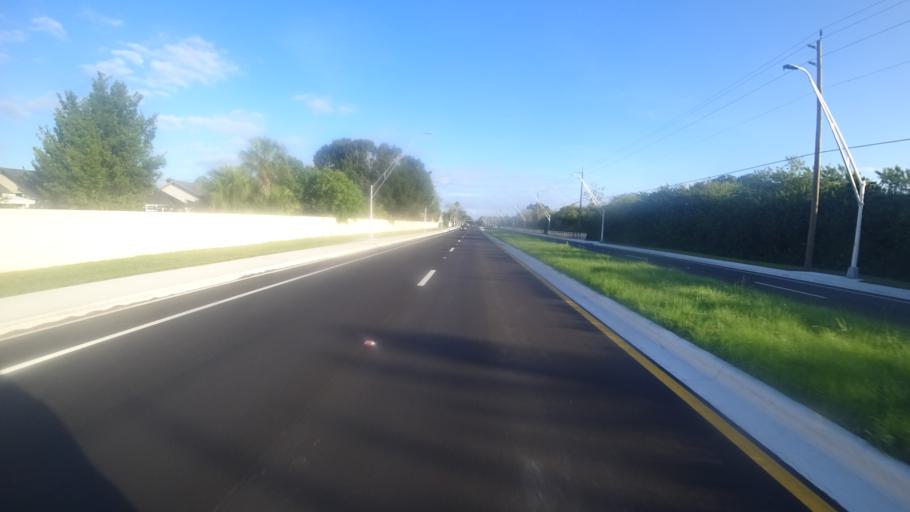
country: US
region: Florida
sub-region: Manatee County
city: Samoset
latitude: 27.4593
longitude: -82.5073
